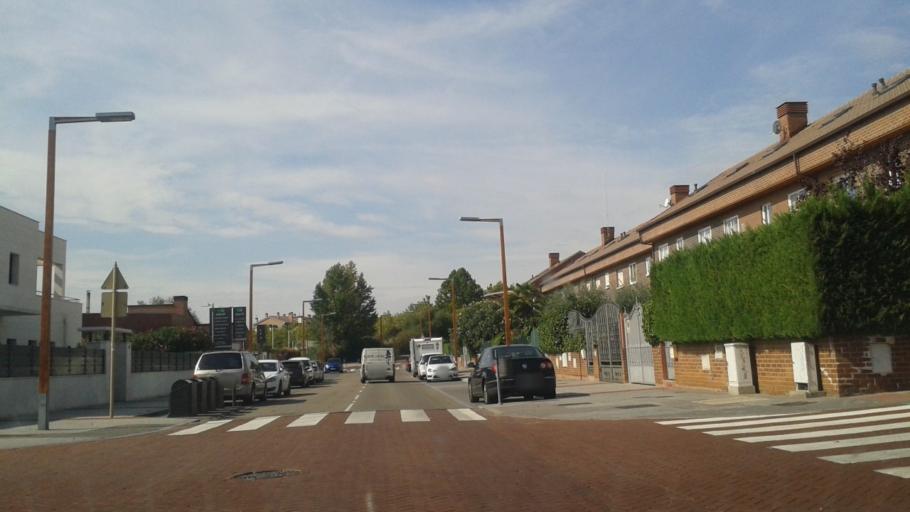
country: ES
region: Castille and Leon
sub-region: Provincia de Valladolid
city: Arroyo
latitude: 41.6115
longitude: -4.7896
